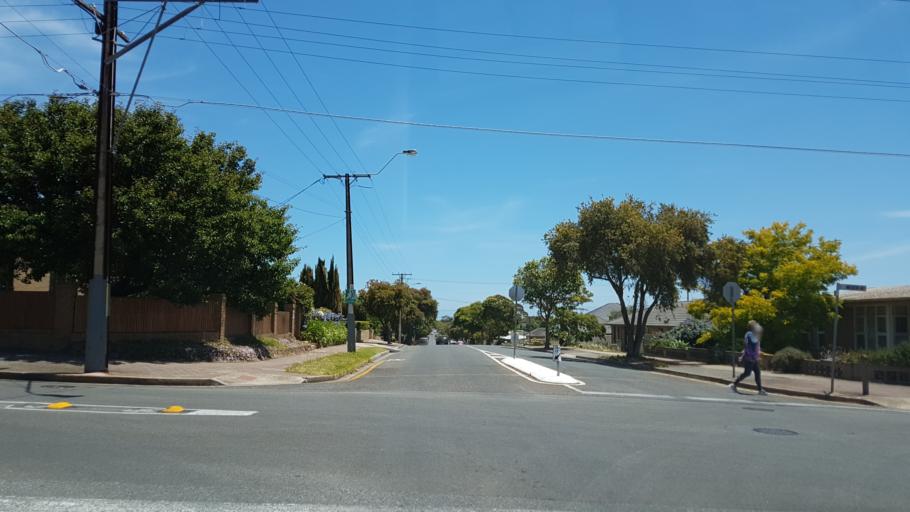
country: AU
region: South Australia
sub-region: Holdfast Bay
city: Seacliff Park
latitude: -35.0257
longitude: 138.5328
